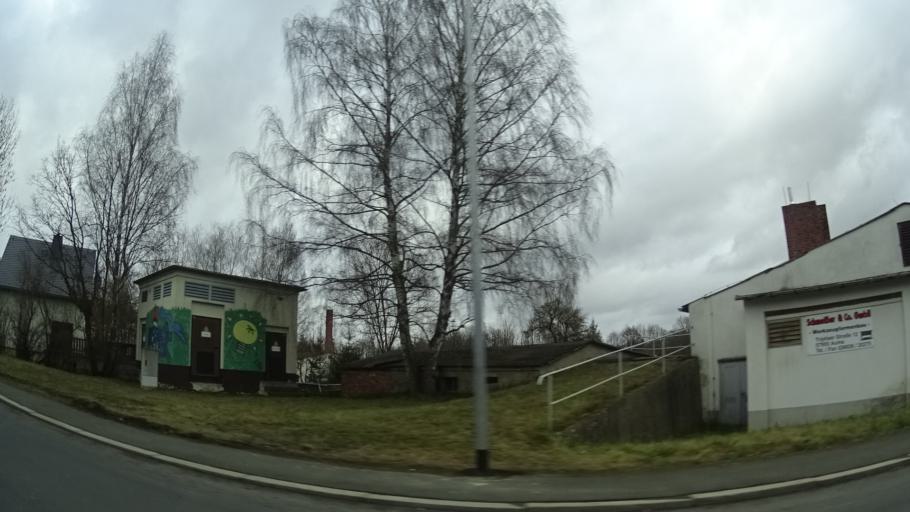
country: DE
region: Thuringia
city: Auma
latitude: 50.7039
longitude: 11.8950
